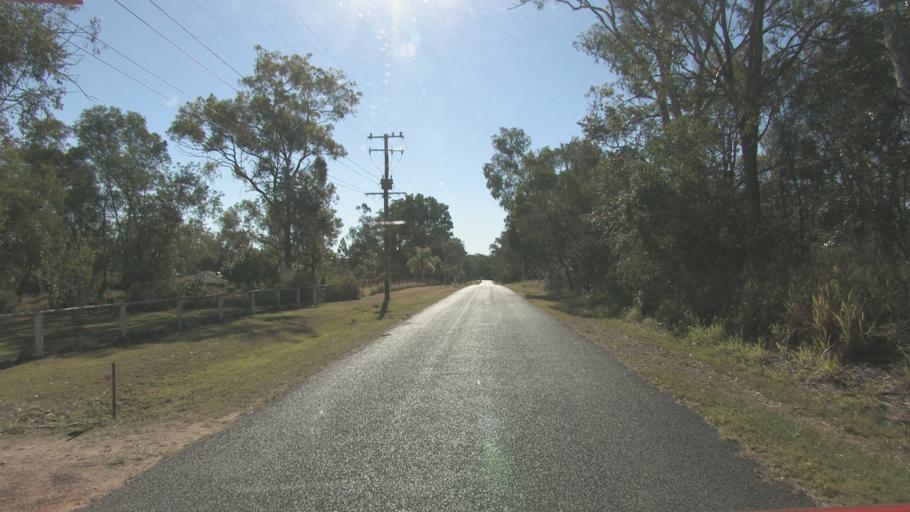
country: AU
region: Queensland
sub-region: Logan
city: Chambers Flat
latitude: -27.7467
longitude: 153.0844
